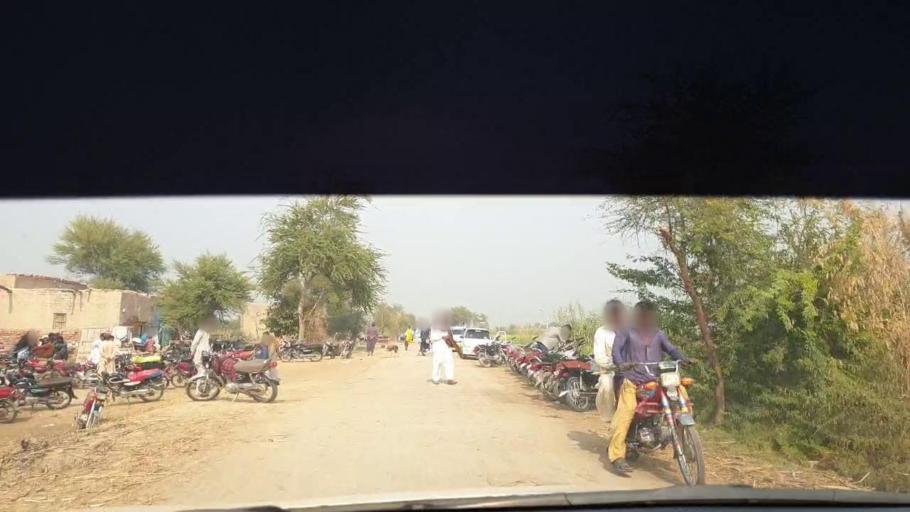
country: PK
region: Sindh
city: Berani
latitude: 25.8048
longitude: 68.8363
